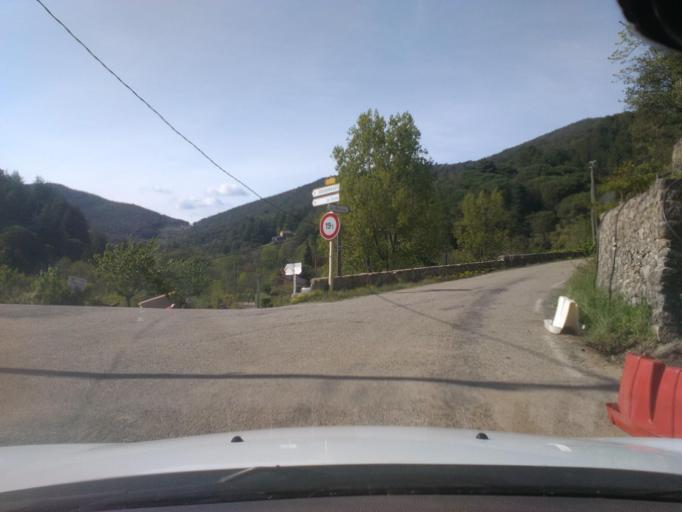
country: FR
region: Languedoc-Roussillon
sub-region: Departement du Gard
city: Lasalle
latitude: 44.0682
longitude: 3.8334
